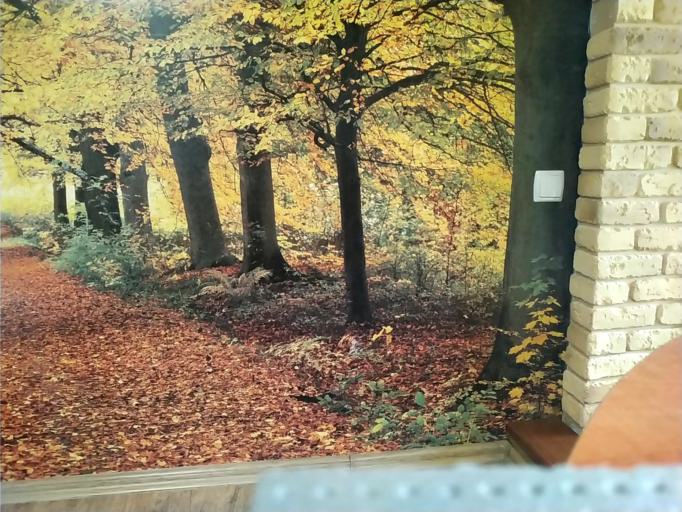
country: RU
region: Tverskaya
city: Staritsa
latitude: 56.5062
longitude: 35.1678
